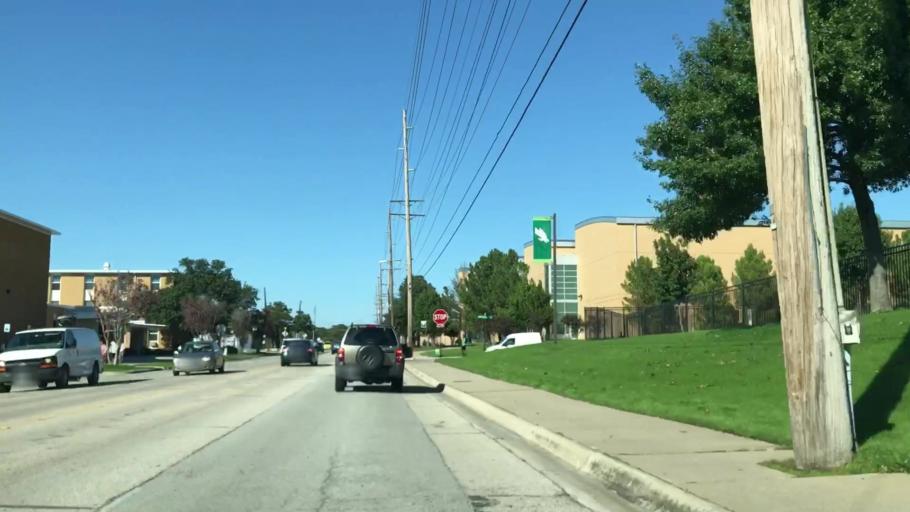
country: US
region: Texas
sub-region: Denton County
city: Denton
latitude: 33.2110
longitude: -97.1550
